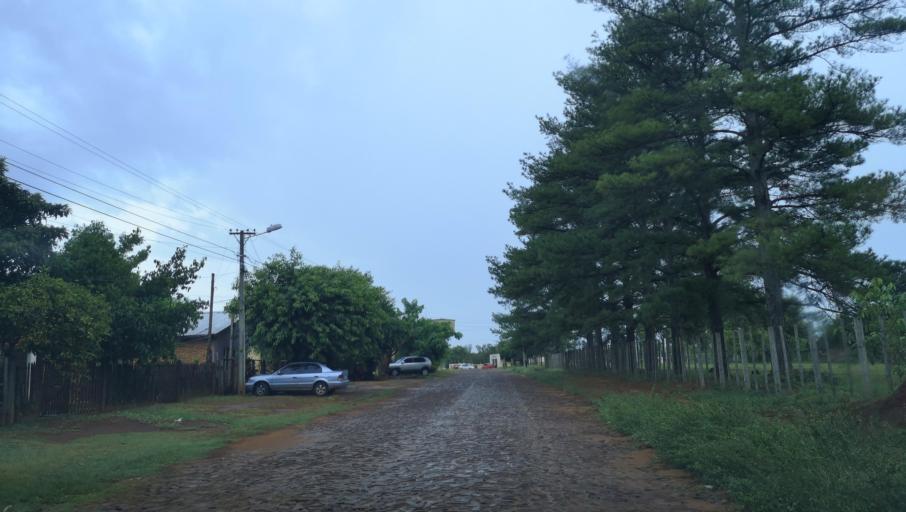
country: PY
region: Misiones
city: Santa Maria
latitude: -26.8946
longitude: -57.0292
